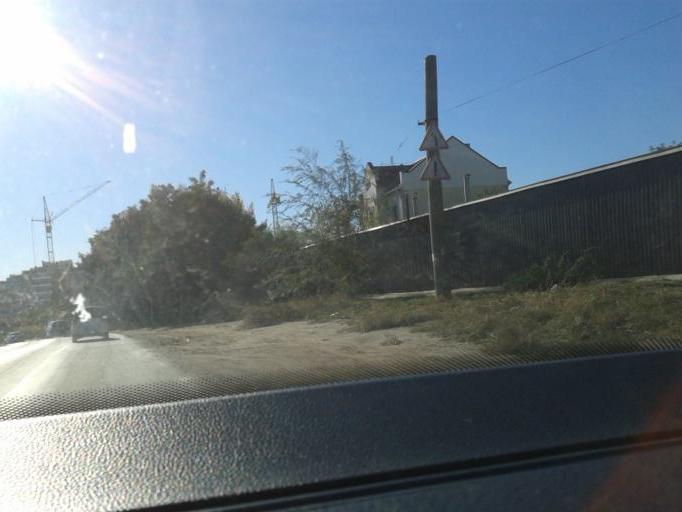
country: RU
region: Volgograd
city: Volgograd
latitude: 48.7684
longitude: 44.5083
